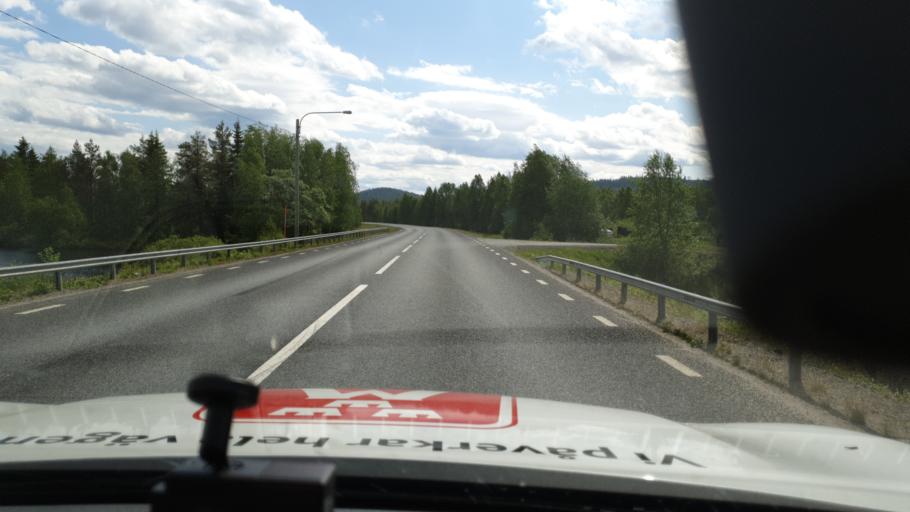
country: SE
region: Vaesterbotten
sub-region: Sorsele Kommun
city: Sorsele
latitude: 65.5123
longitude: 17.5399
